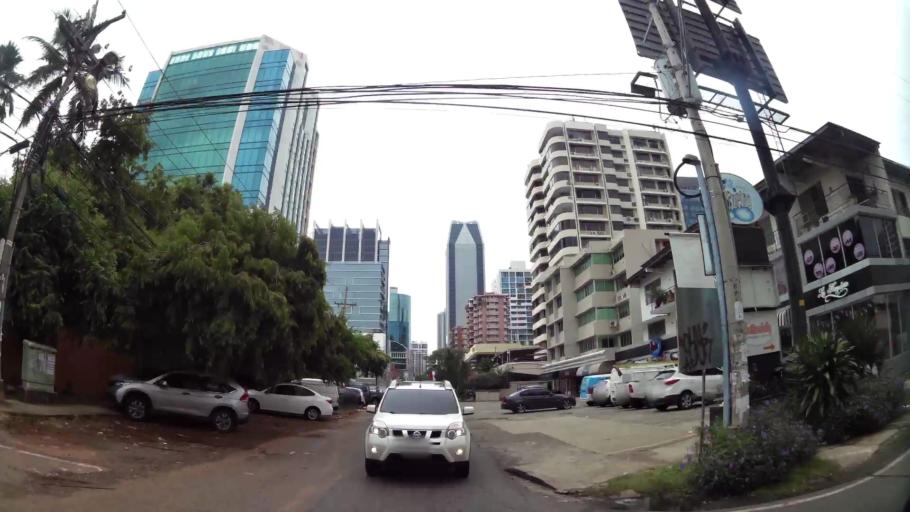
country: PA
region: Panama
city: Panama
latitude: 8.9875
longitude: -79.5181
